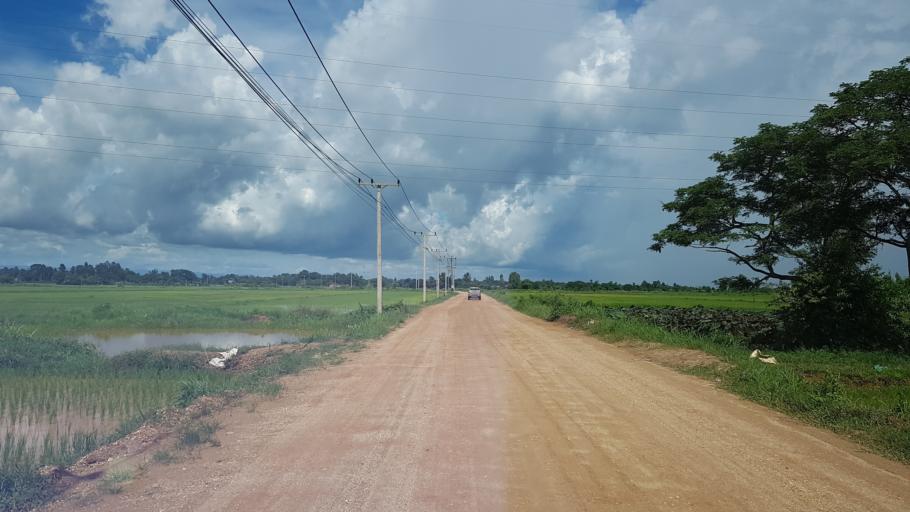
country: LA
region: Vientiane
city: Vientiane
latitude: 18.2154
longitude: 102.5026
